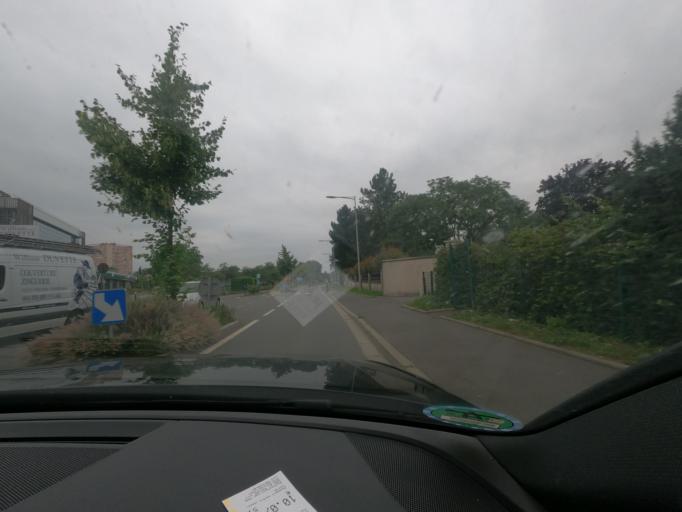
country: FR
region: Picardie
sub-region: Departement de la Somme
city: Amiens
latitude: 49.8695
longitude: 2.3076
